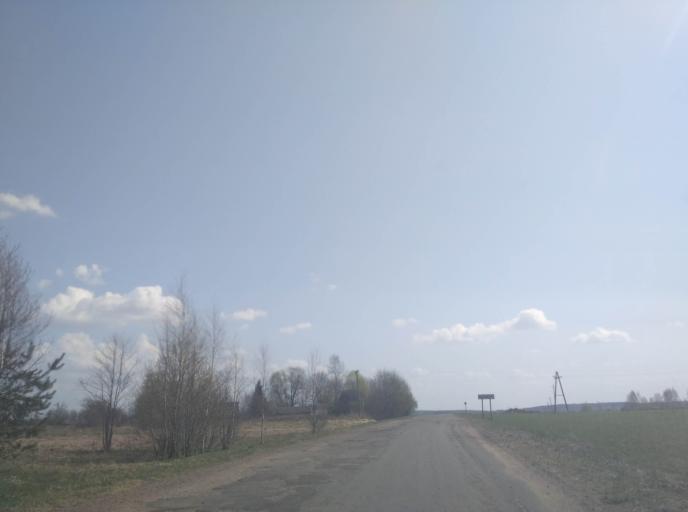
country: BY
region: Minsk
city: Loshnitsa
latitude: 54.4917
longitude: 28.7228
